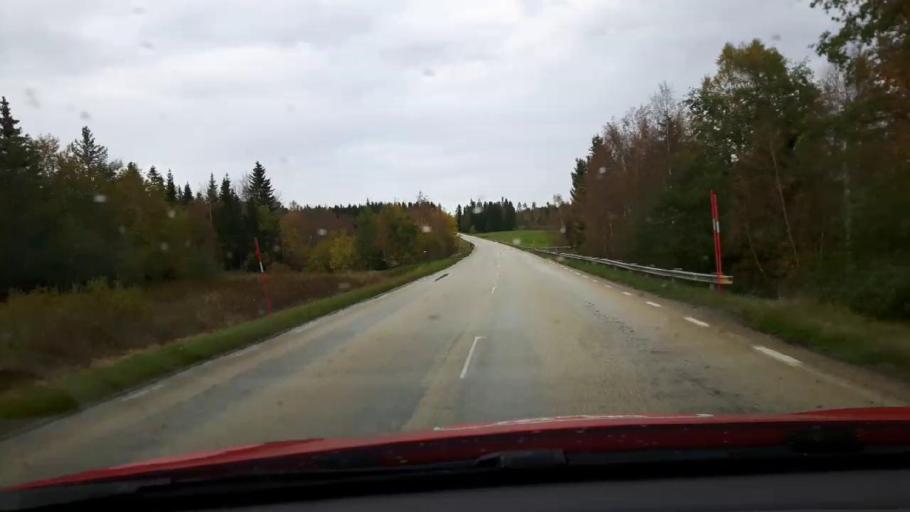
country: SE
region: Jaemtland
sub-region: Bergs Kommun
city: Hoverberg
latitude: 62.9757
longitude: 14.3478
